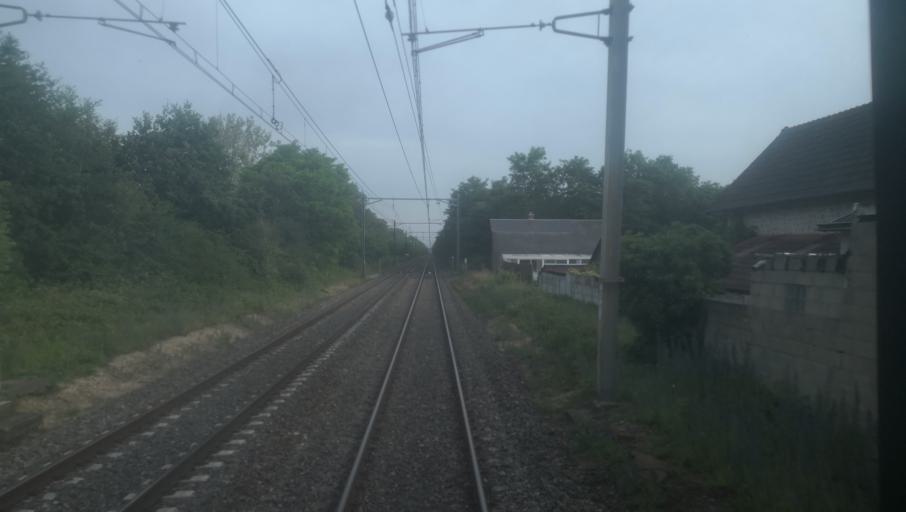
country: FR
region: Centre
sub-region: Departement du Loiret
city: Menestreau-en-Villette
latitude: 47.6509
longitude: 1.9819
